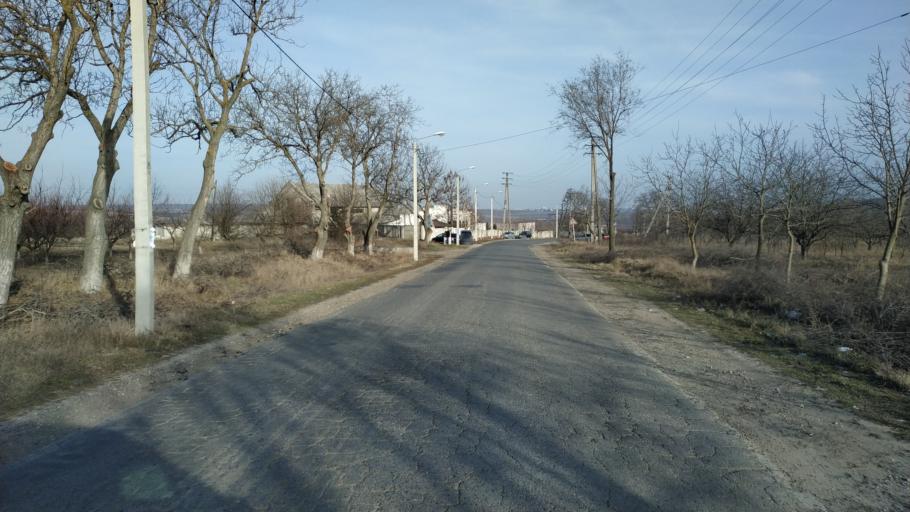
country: MD
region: Chisinau
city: Vatra
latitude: 47.0715
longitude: 28.7112
